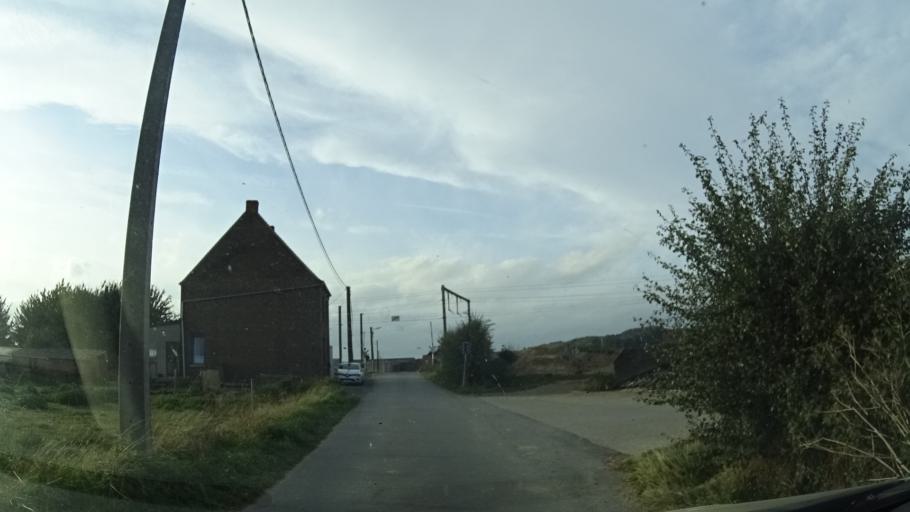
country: BE
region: Wallonia
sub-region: Province du Hainaut
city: Frasnes-lez-Buissenal
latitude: 50.5922
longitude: 3.5890
